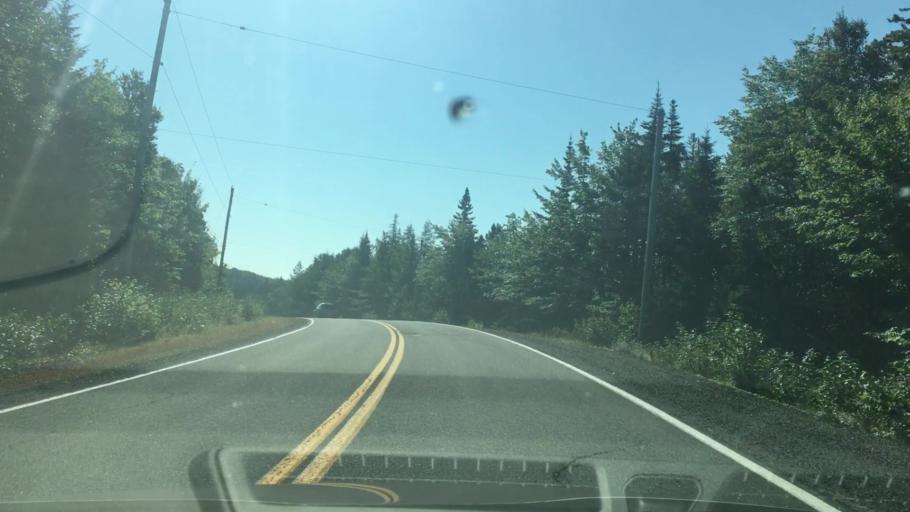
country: CA
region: Nova Scotia
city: Cole Harbour
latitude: 44.8084
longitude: -62.8342
